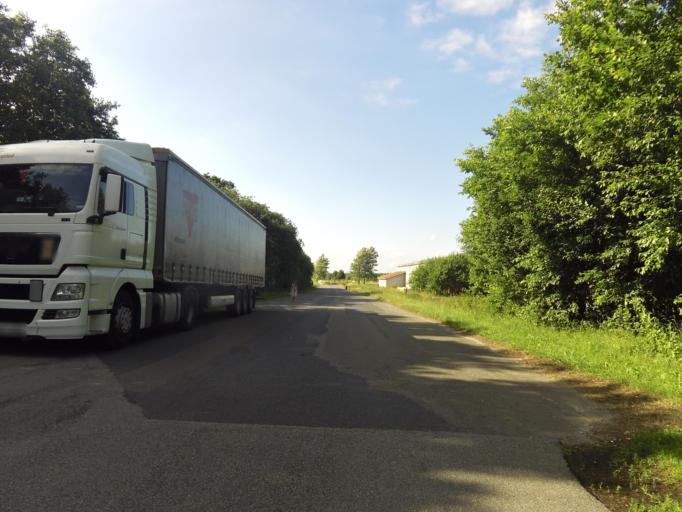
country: DK
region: South Denmark
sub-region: Vejen Kommune
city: Rodding
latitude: 55.3773
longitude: 9.0558
